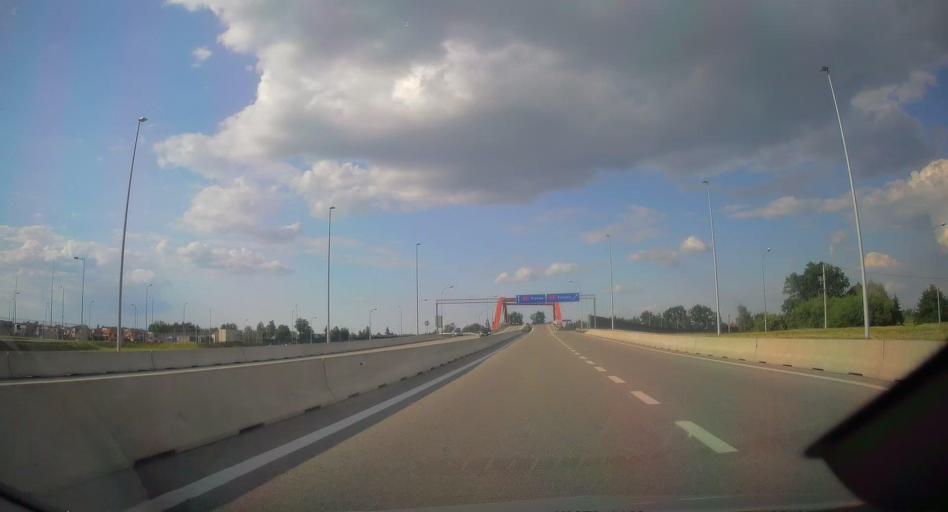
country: PL
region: Subcarpathian Voivodeship
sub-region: Powiat debicki
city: Zyrakow
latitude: 50.0770
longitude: 21.3834
